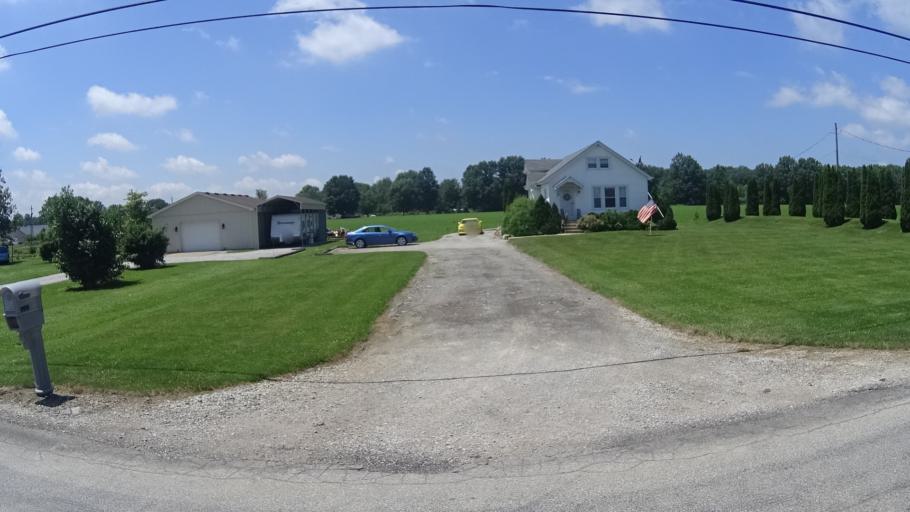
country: US
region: Ohio
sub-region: Huron County
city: Wakeman
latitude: 41.3293
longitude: -82.3738
